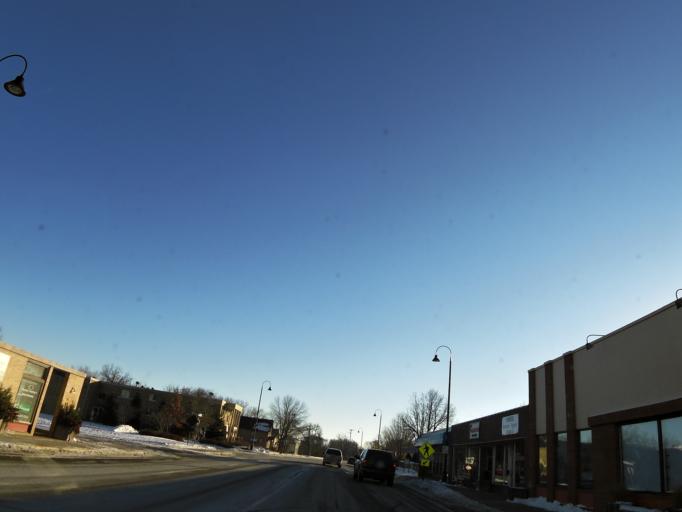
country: US
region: Minnesota
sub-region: Hennepin County
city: Mound
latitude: 44.9366
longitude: -93.6664
